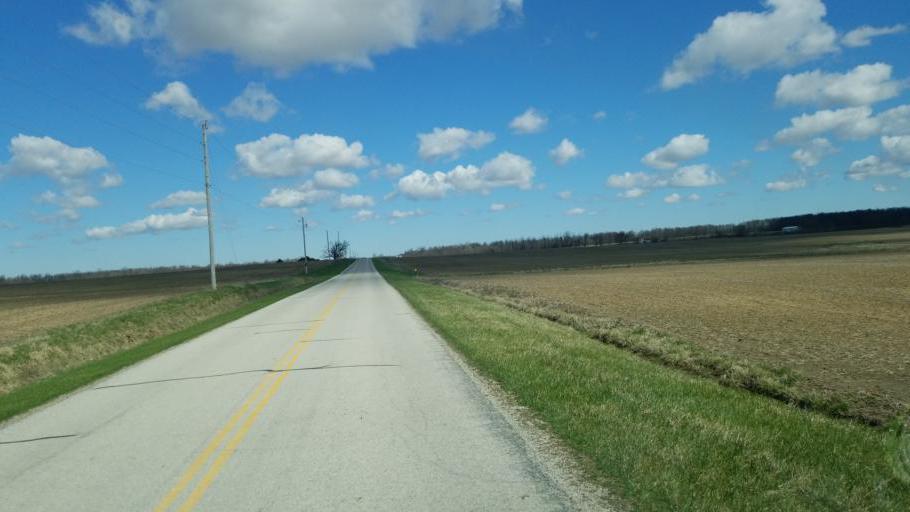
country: US
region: Ohio
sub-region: Sandusky County
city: Mount Carmel
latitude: 41.1395
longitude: -82.9383
